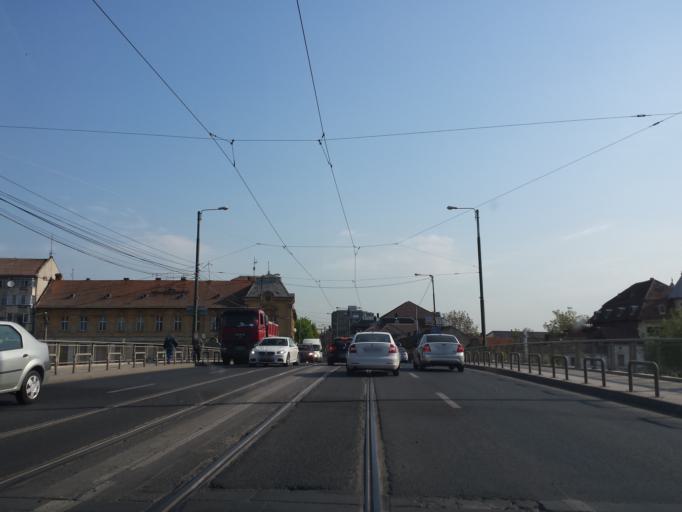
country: RO
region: Timis
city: Timisoara
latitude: 45.7597
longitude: 21.2587
